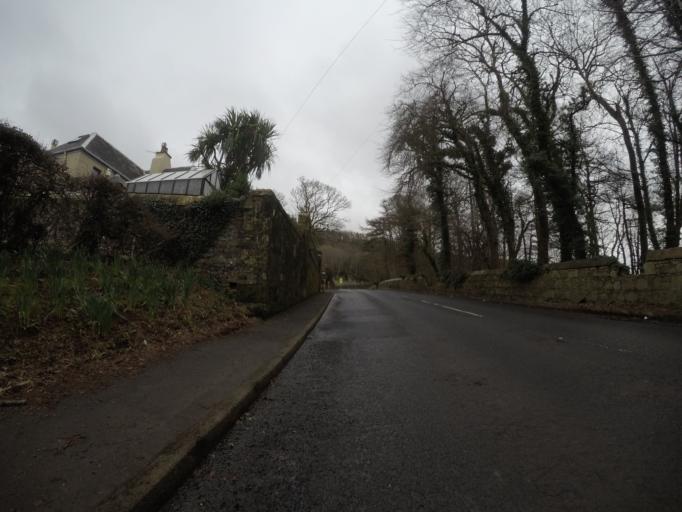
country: GB
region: Scotland
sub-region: North Ayrshire
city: Largs
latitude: 55.7846
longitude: -4.8556
